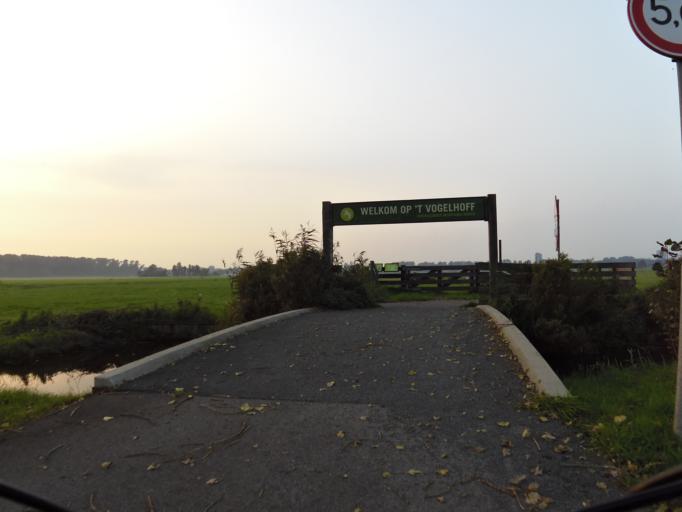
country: NL
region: South Holland
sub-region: Gemeente Voorschoten
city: Voorschoten
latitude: 52.1252
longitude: 4.4811
